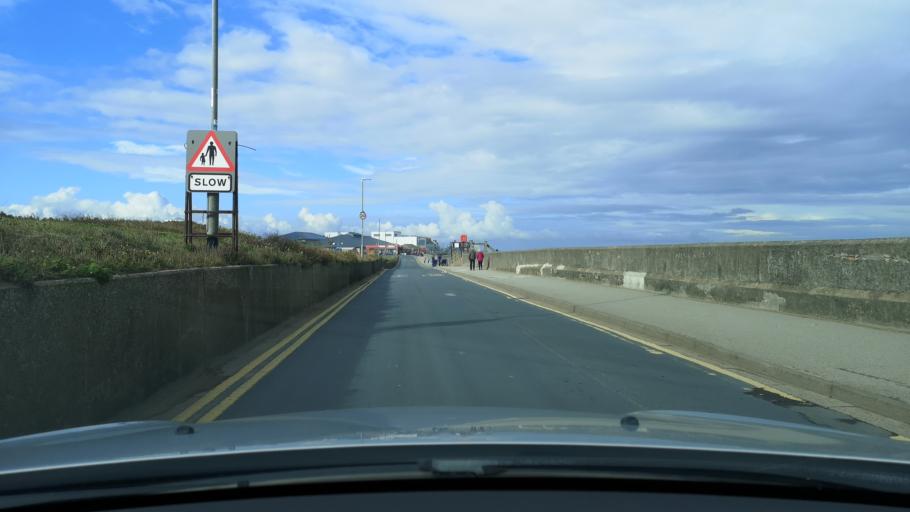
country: GB
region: England
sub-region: East Riding of Yorkshire
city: Hornsea
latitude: 53.9097
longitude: -0.1590
